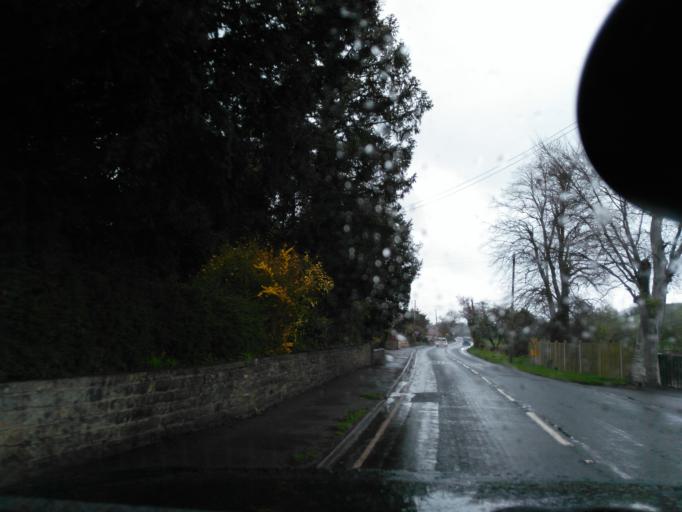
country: GB
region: England
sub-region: Somerset
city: Street
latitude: 51.1232
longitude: -2.8220
